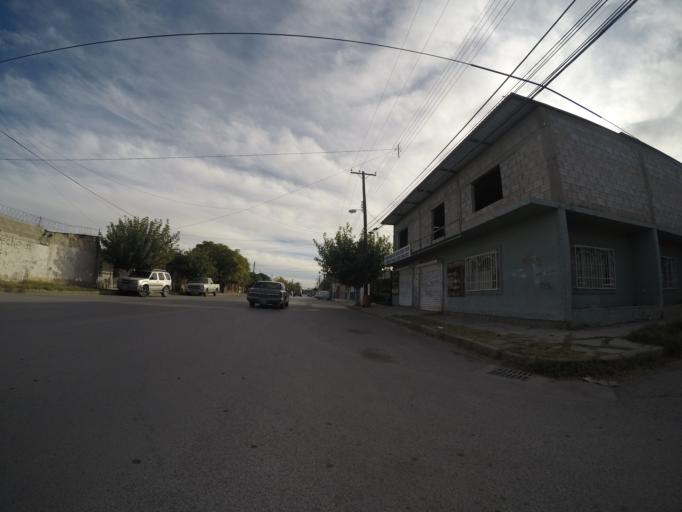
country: MX
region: Chihuahua
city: Ciudad Juarez
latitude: 31.7293
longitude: -106.4278
